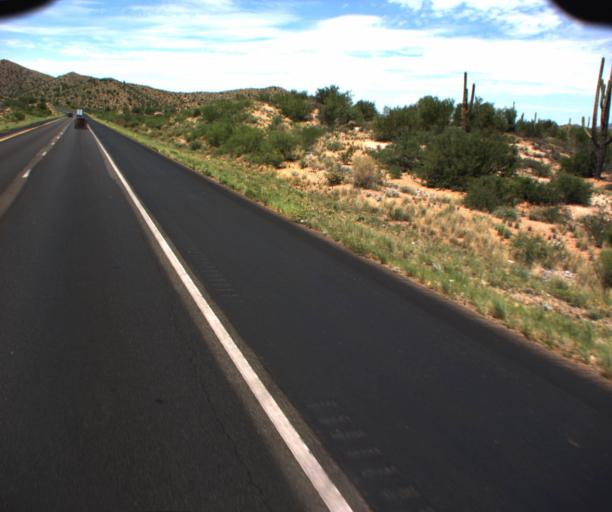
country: US
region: Arizona
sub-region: Pinal County
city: Superior
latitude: 33.2732
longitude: -111.1939
